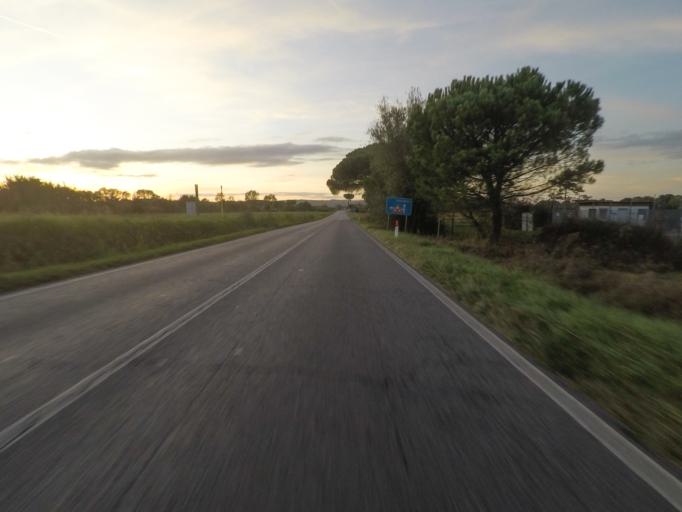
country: IT
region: Tuscany
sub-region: Provincia di Siena
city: Torrita di Siena
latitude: 43.1882
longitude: 11.7604
